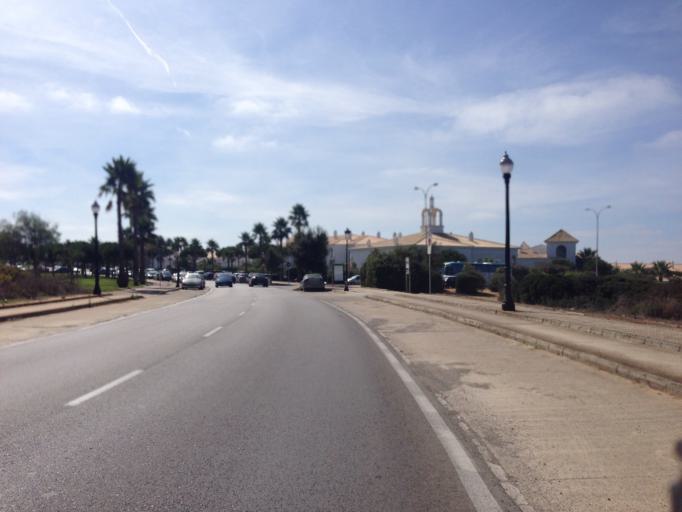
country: ES
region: Andalusia
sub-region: Provincia de Cadiz
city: Chiclana de la Frontera
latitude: 36.3395
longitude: -6.1598
